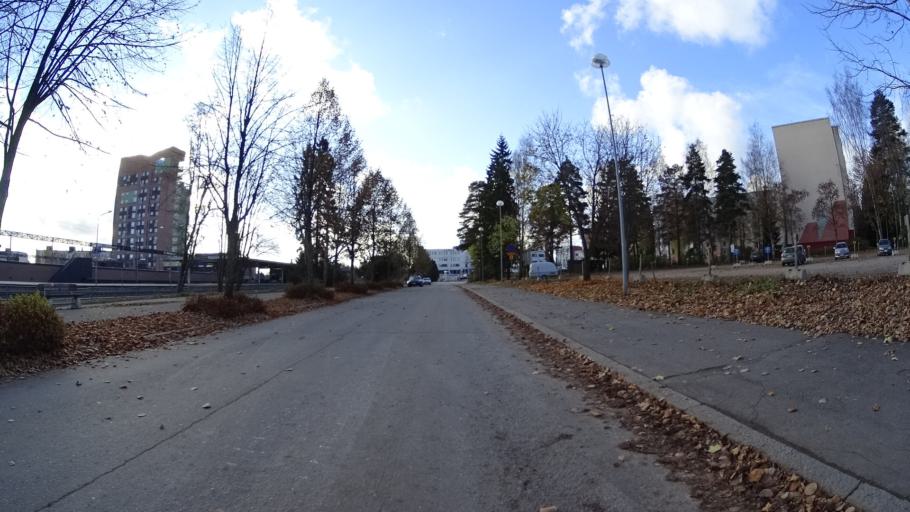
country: FI
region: Uusimaa
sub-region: Helsinki
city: Teekkarikylae
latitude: 60.2792
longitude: 24.8524
